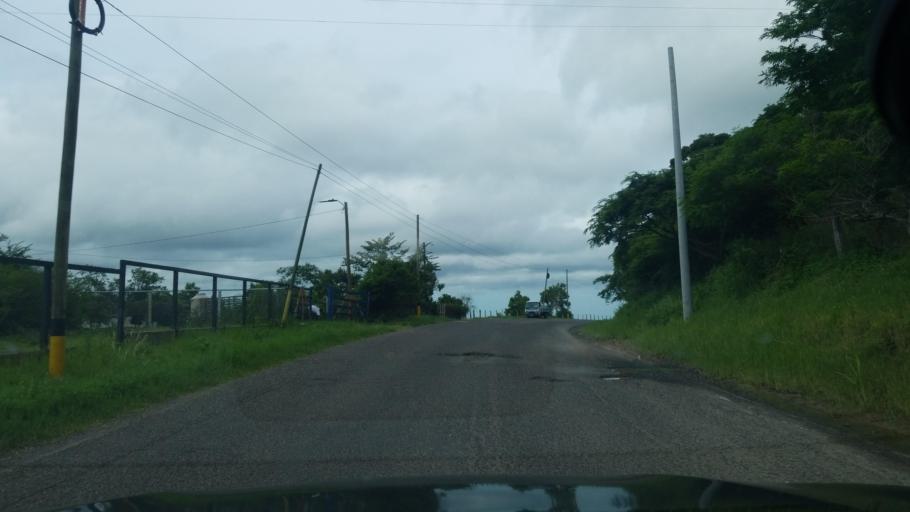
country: HN
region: Choluteca
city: Corpus
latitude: 13.3713
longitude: -86.9485
